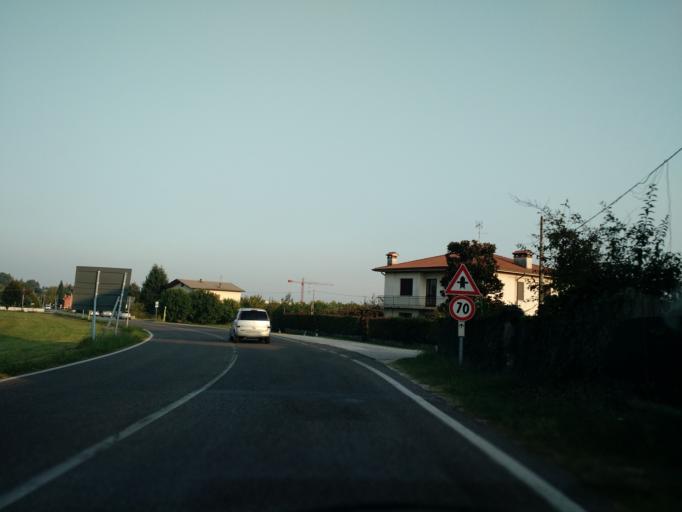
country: IT
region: Veneto
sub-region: Provincia di Vicenza
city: Sarcedo
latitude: 45.7013
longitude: 11.5146
